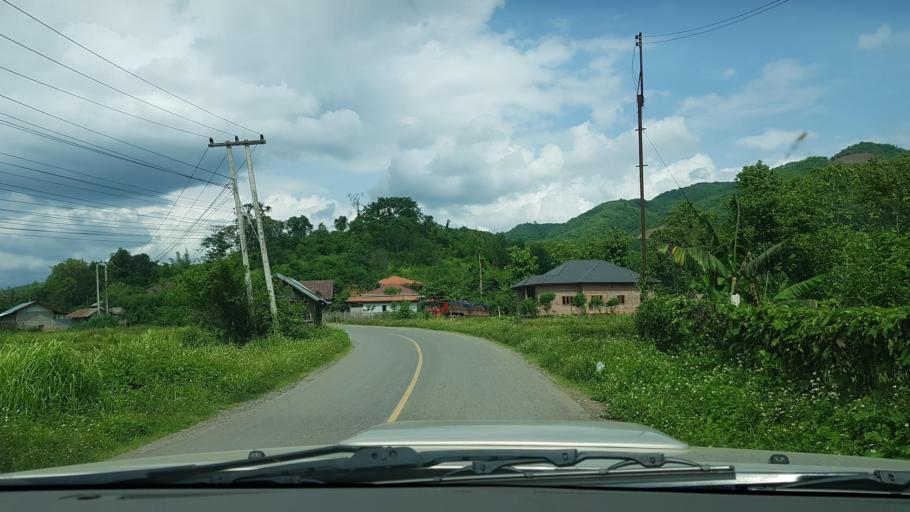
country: LA
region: Loungnamtha
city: Muang Nale
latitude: 20.2506
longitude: 101.5818
